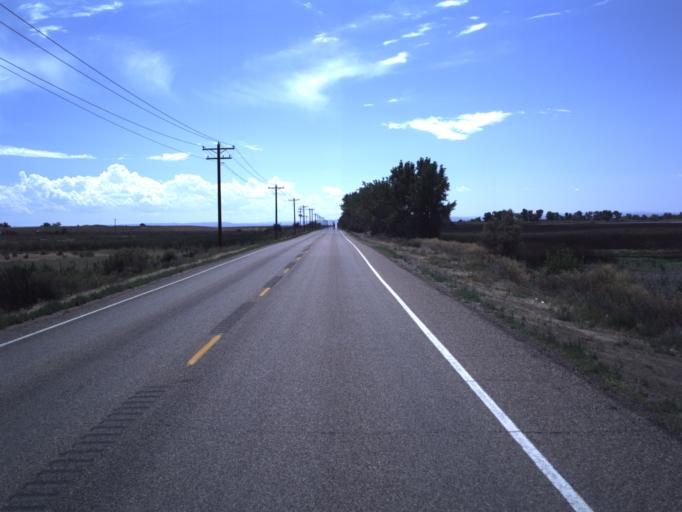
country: US
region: Utah
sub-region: Uintah County
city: Naples
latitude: 40.1981
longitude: -109.6648
